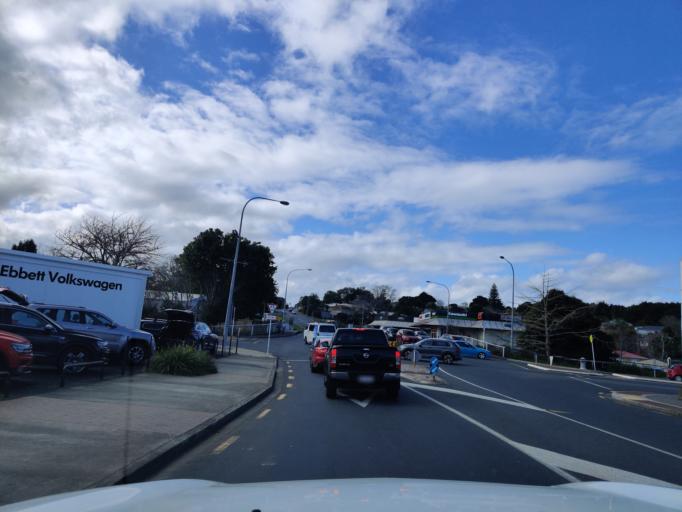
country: NZ
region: Auckland
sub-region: Auckland
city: Pukekohe East
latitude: -37.2016
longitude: 174.9075
